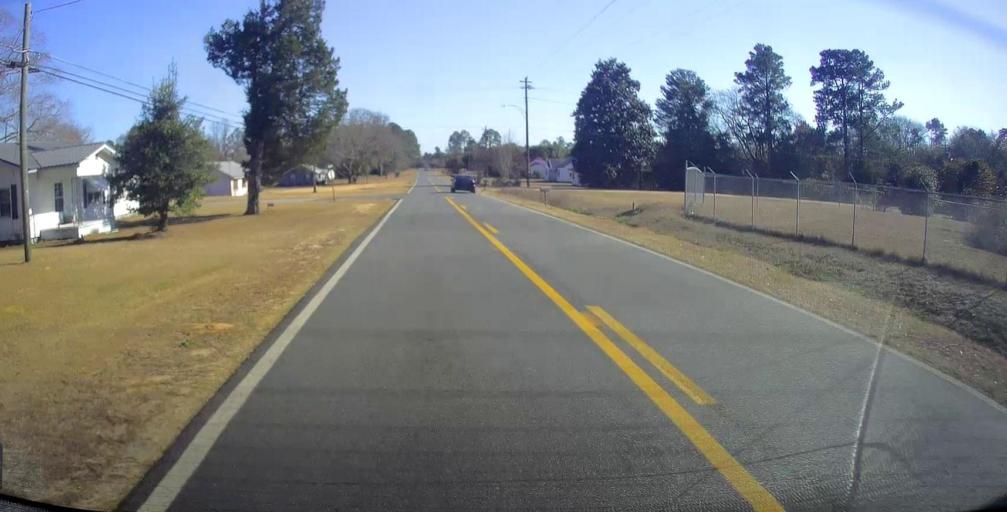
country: US
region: Georgia
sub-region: Taylor County
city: Butler
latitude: 32.5524
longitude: -84.2308
